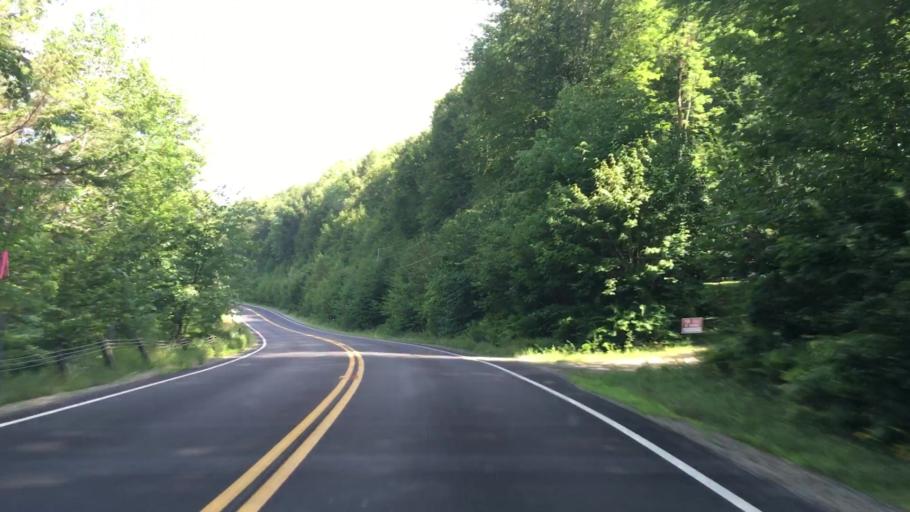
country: US
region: New Hampshire
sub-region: Grafton County
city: North Haverhill
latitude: 44.1169
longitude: -71.9144
